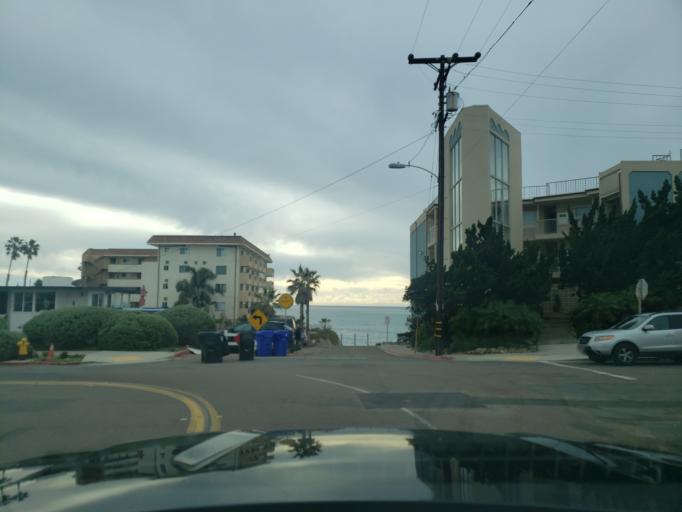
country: US
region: California
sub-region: San Diego County
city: Coronado
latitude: 32.7400
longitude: -117.2544
